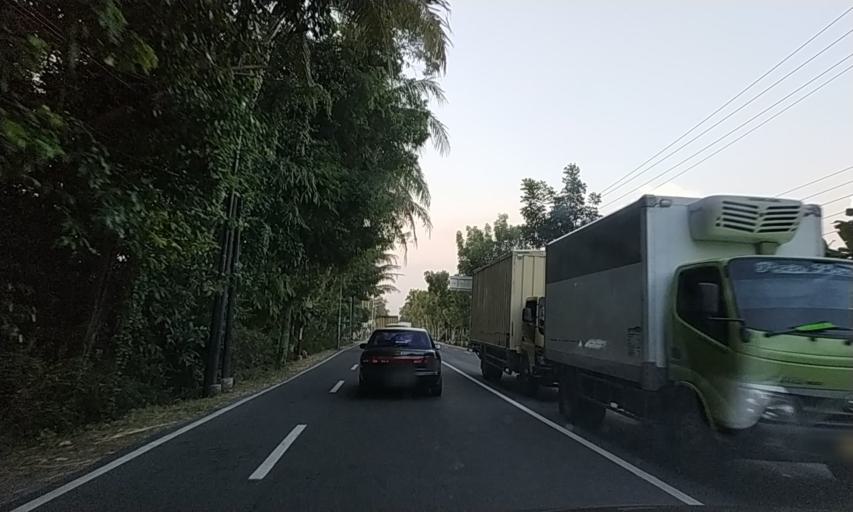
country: ID
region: Daerah Istimewa Yogyakarta
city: Srandakan
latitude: -7.8912
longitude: 110.1294
